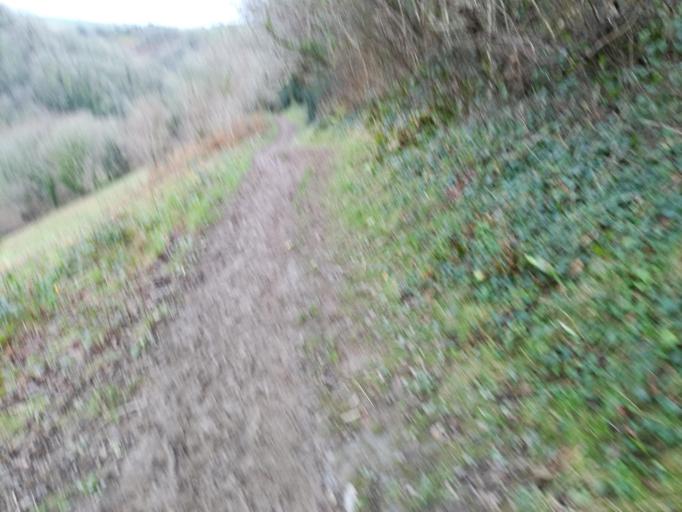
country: GB
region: England
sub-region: Cornwall
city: Fowey
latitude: 50.3352
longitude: -4.6131
